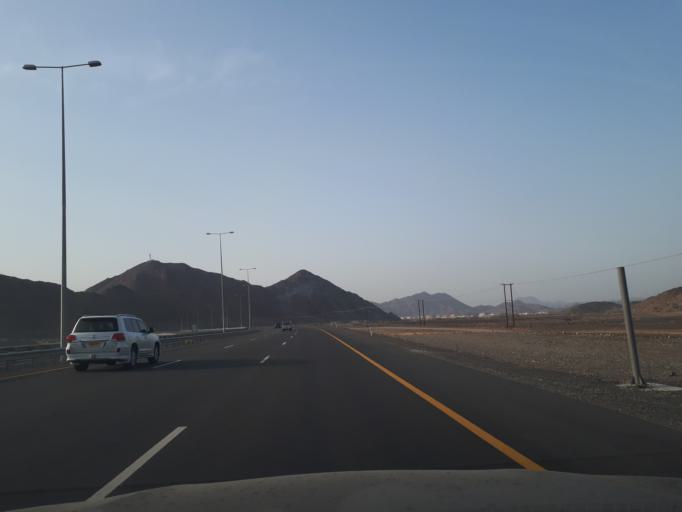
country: OM
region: Muhafazat ad Dakhiliyah
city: Sufalat Sama'il
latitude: 23.3035
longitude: 58.1110
